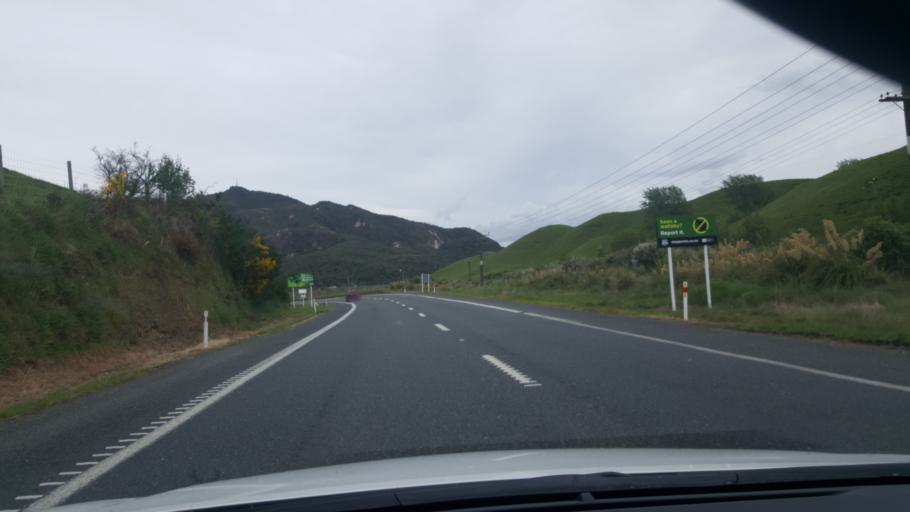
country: NZ
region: Bay of Plenty
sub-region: Rotorua District
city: Rotorua
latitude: -38.3051
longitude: 176.3703
